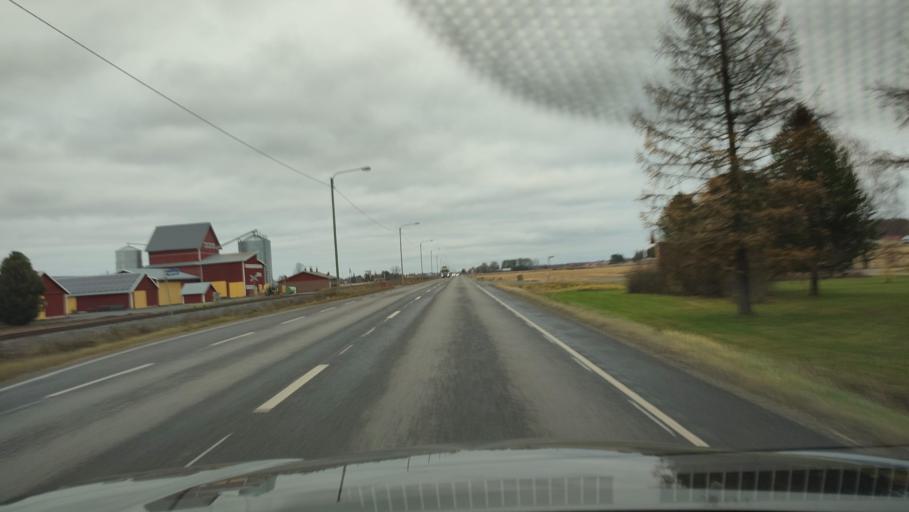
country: FI
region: Southern Ostrobothnia
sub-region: Seinaejoki
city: Ilmajoki
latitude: 62.7076
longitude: 22.5306
